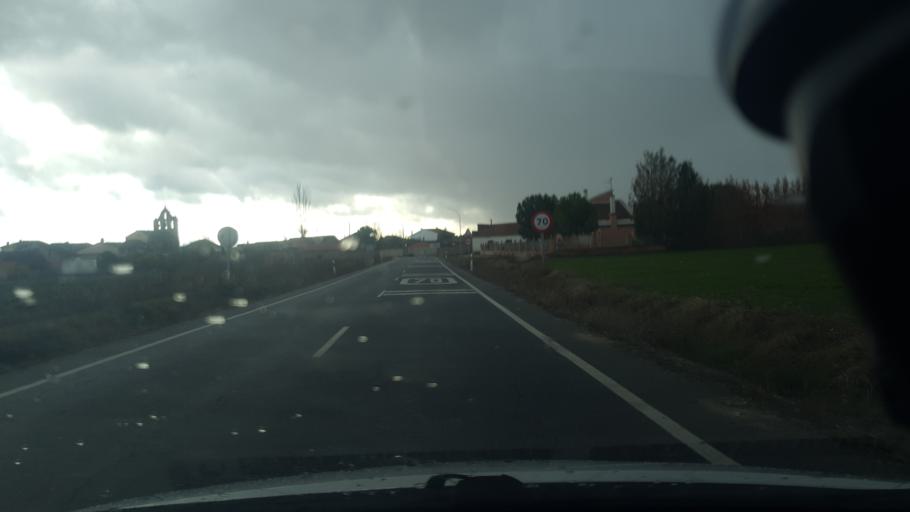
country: ES
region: Castille and Leon
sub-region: Provincia de Segovia
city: Chane
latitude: 41.3021
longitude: -4.4045
